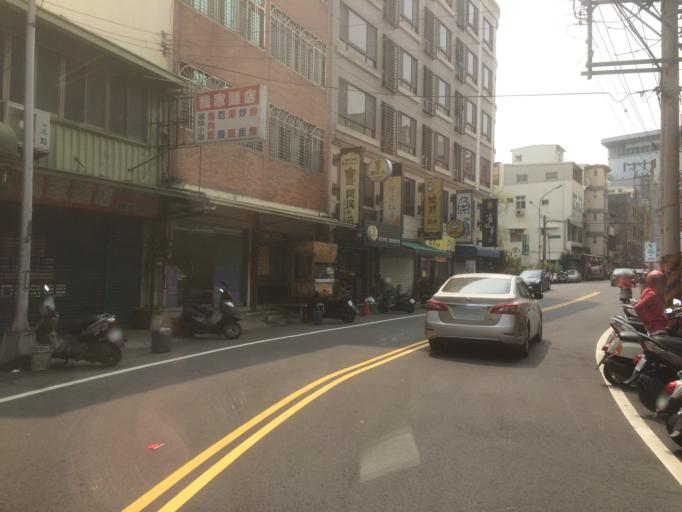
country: TW
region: Taiwan
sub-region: Hsinchu
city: Hsinchu
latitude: 24.7948
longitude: 120.9626
